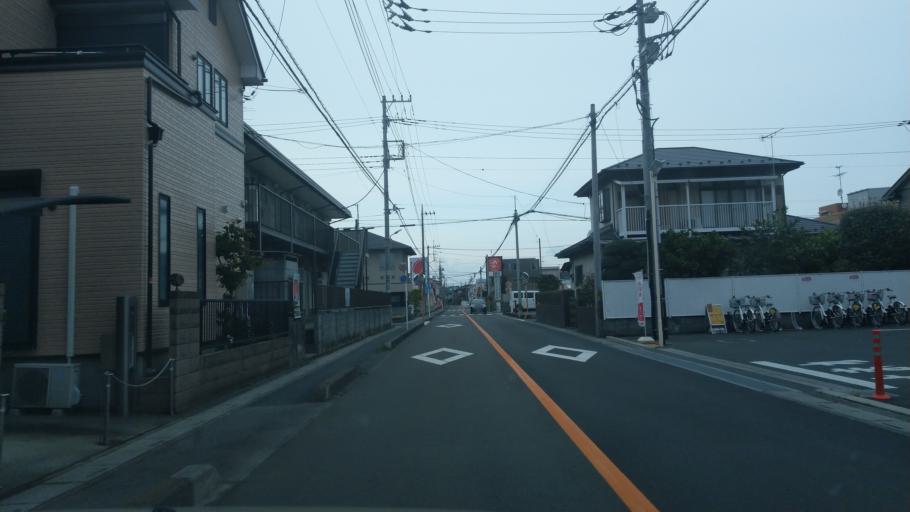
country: JP
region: Saitama
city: Ageoshimo
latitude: 35.9458
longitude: 139.6029
